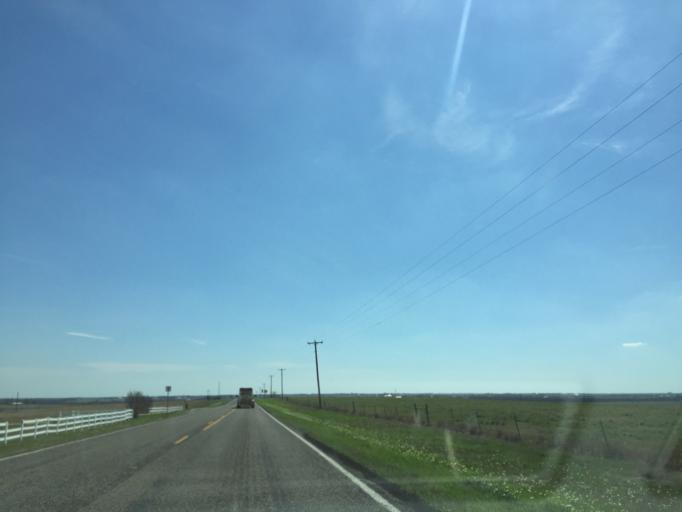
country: US
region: Texas
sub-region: Williamson County
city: Taylor
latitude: 30.5582
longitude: -97.3246
